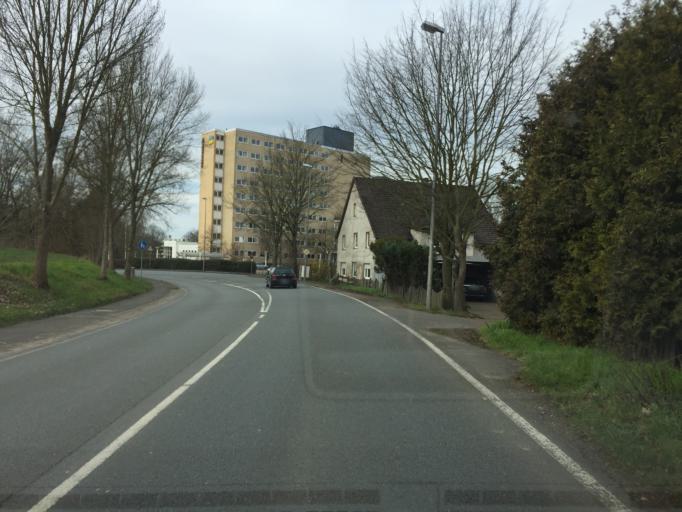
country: DE
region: North Rhine-Westphalia
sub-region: Regierungsbezirk Detmold
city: Bad Salzuflen
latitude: 52.0943
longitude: 8.7634
